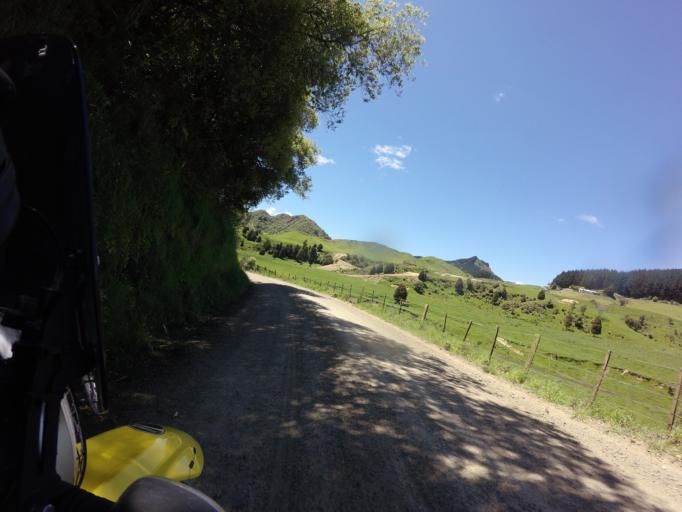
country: NZ
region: Bay of Plenty
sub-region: Opotiki District
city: Opotiki
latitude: -38.3927
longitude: 177.4596
